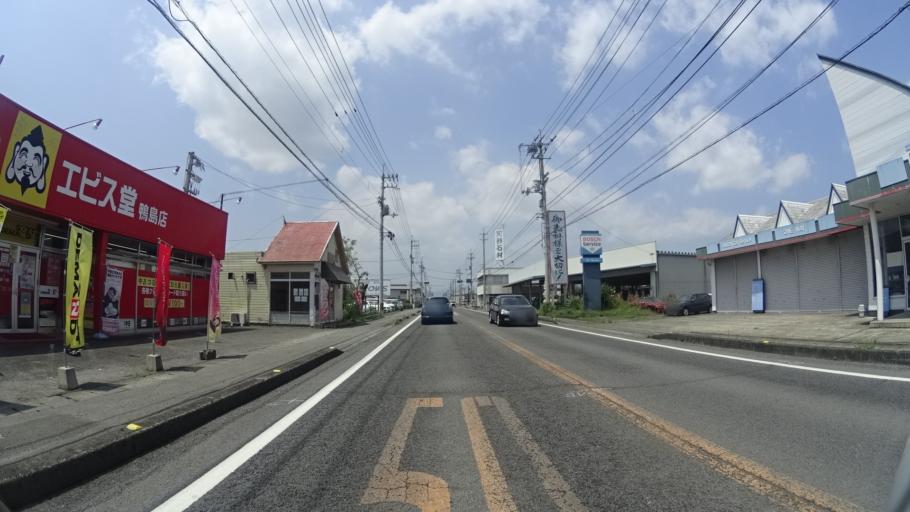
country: JP
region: Tokushima
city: Ishii
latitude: 34.0717
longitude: 134.3990
